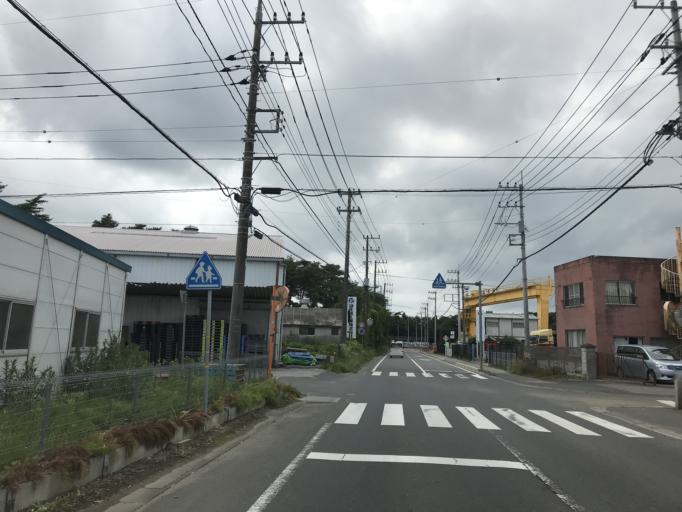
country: JP
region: Ibaraki
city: Ushiku
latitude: 35.9787
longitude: 140.0720
